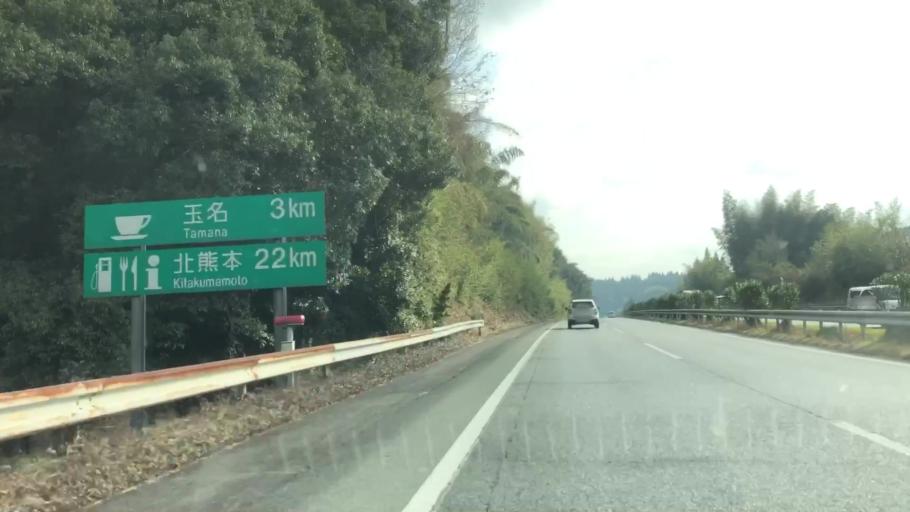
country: JP
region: Kumamoto
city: Yamaga
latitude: 33.0373
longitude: 130.5711
